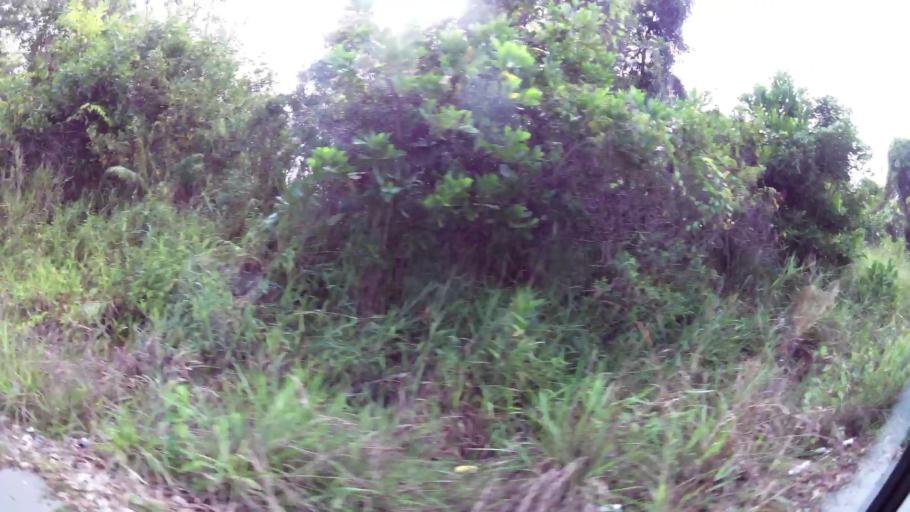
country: BN
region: Brunei and Muara
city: Bandar Seri Begawan
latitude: 4.8921
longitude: 114.8944
